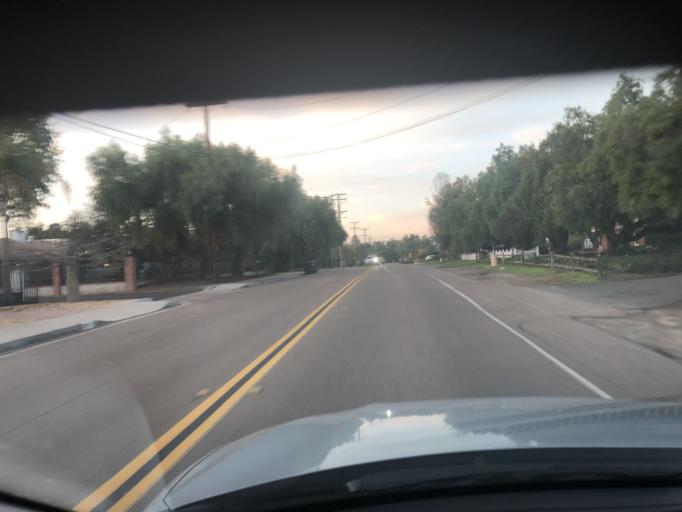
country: US
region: California
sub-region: San Diego County
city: Chula Vista
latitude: 32.6420
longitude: -117.0666
